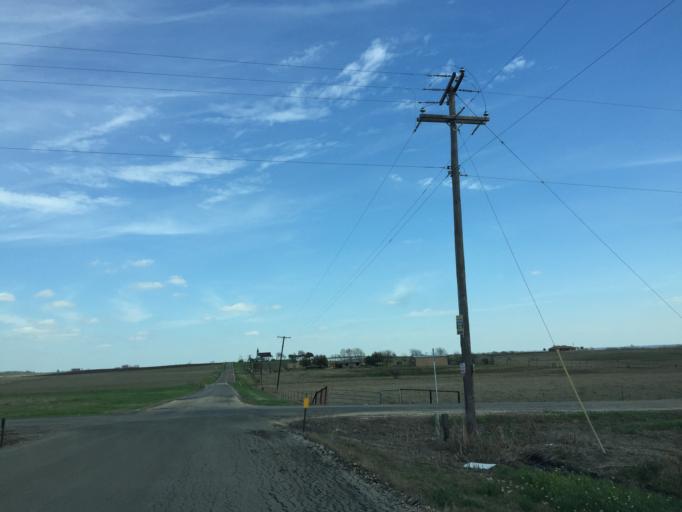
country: US
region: Texas
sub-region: Williamson County
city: Taylor
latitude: 30.5533
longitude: -97.3230
